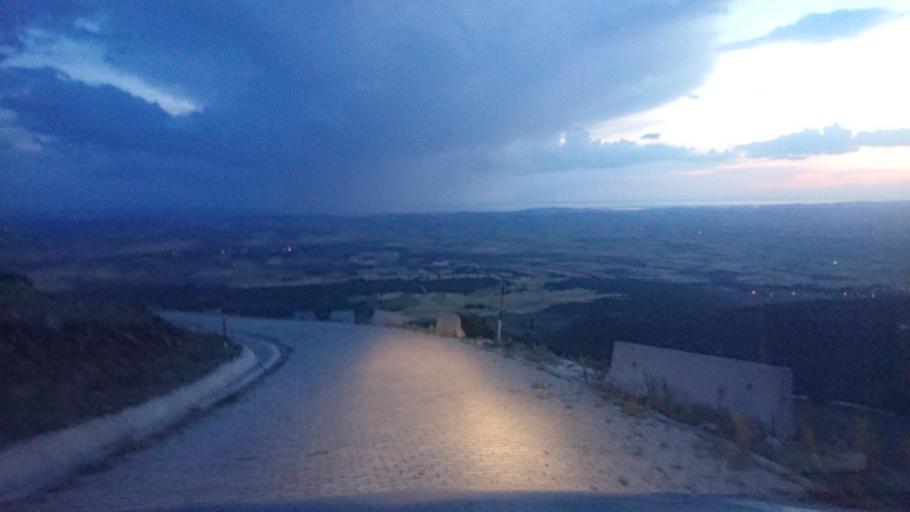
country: TR
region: Aksaray
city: Ortakoy
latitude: 38.6416
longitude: 34.0282
